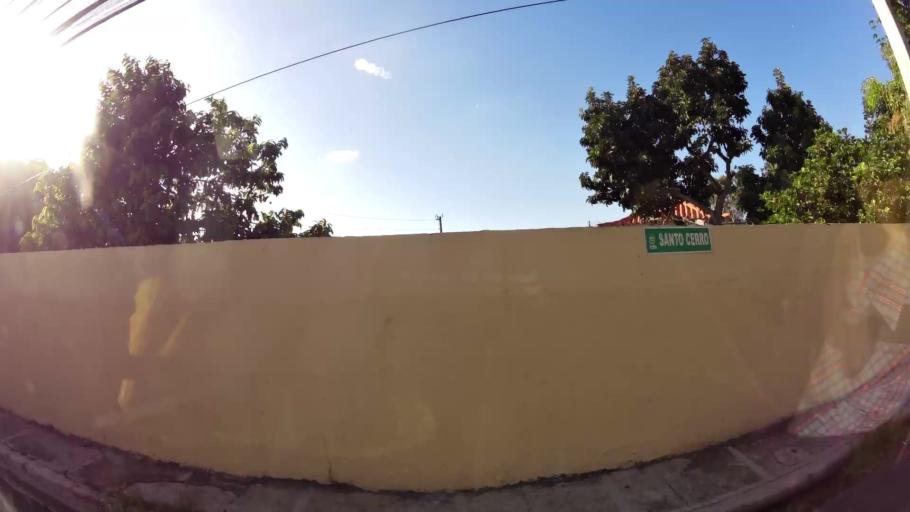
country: DO
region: Nacional
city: Santo Domingo
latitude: 18.4961
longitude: -69.9708
